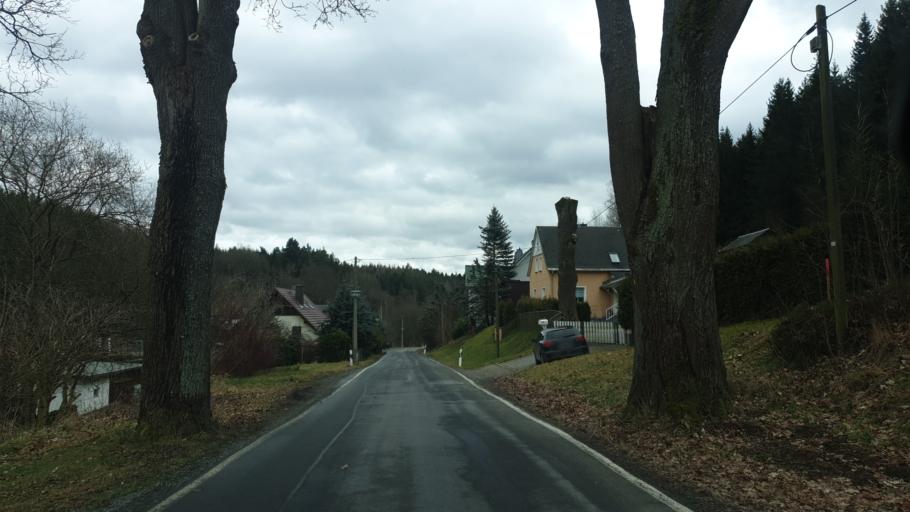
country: DE
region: Saxony
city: Bad Elster
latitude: 50.2920
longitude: 12.2193
